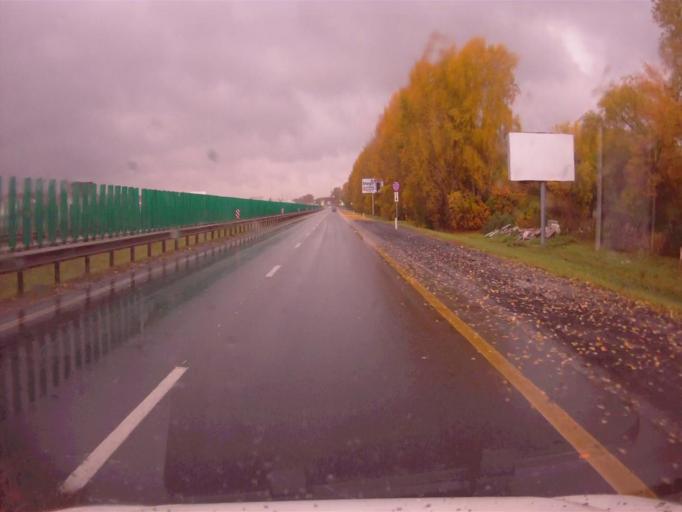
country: RU
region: Chelyabinsk
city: Dolgoderevenskoye
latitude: 55.2789
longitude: 61.3435
